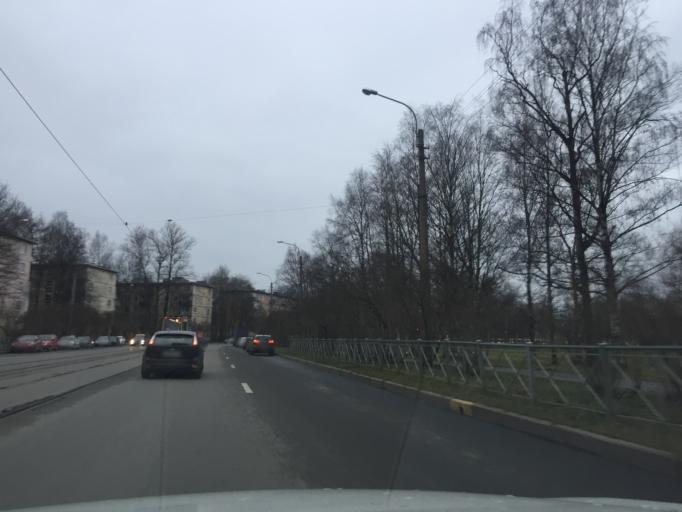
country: RU
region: Leningrad
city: Akademicheskoe
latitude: 60.0174
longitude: 30.3735
